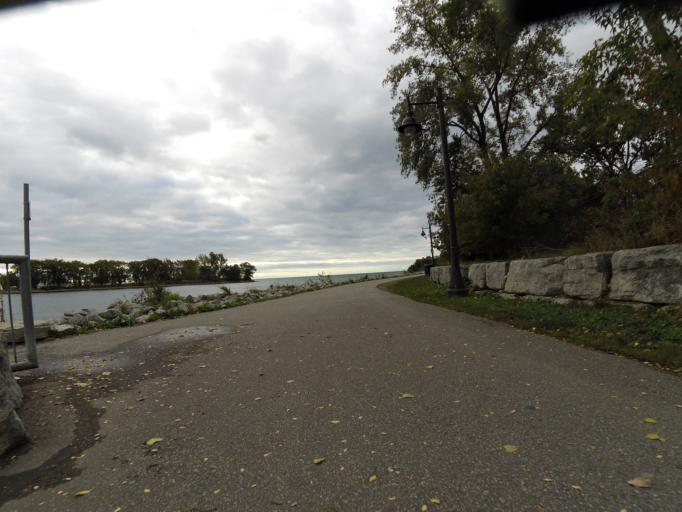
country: CA
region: Ontario
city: Etobicoke
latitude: 43.6159
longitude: -79.4854
